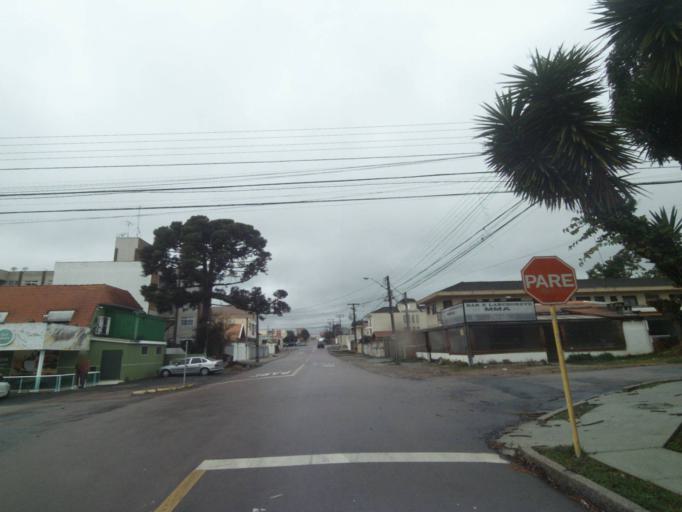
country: BR
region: Parana
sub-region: Sao Jose Dos Pinhais
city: Sao Jose dos Pinhais
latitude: -25.5177
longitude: -49.3007
